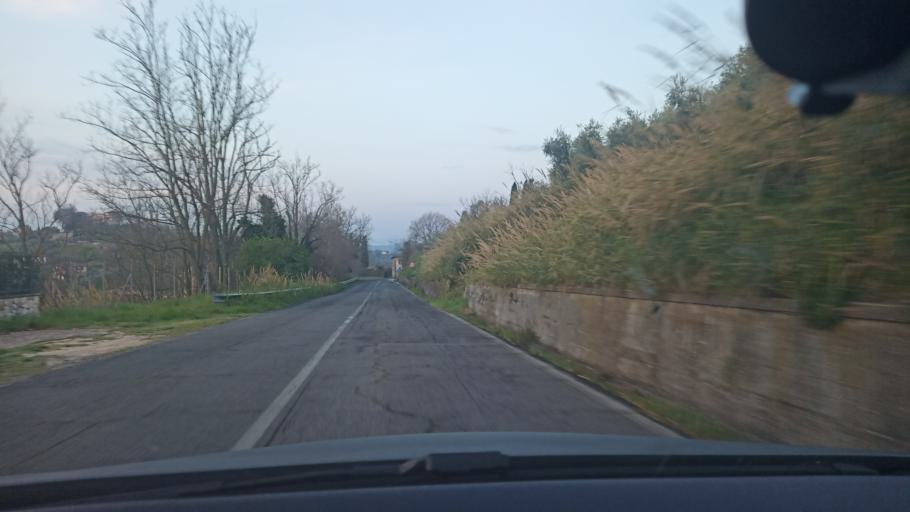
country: IT
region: Latium
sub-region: Provincia di Rieti
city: Torri in Sabina
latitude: 42.3504
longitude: 12.6502
